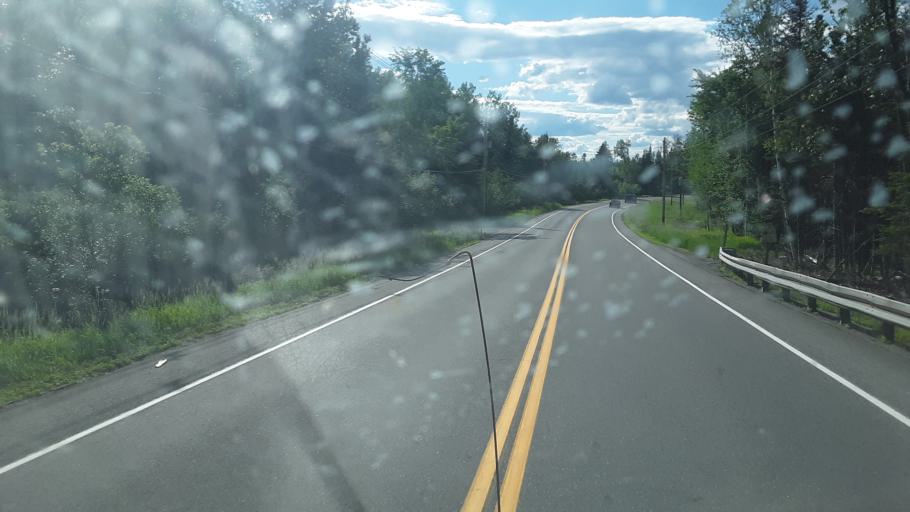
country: US
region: Maine
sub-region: Penobscot County
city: Patten
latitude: 45.8866
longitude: -68.4202
